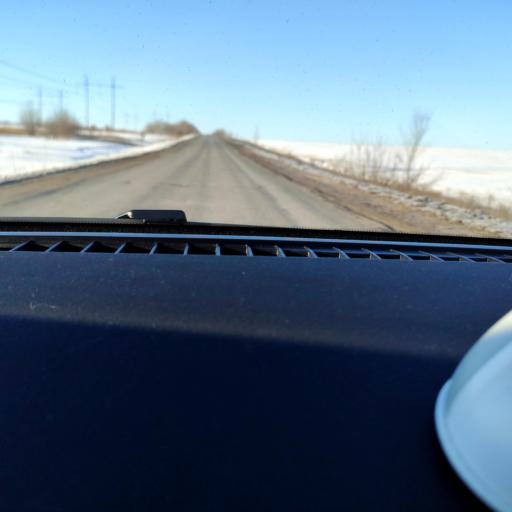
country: RU
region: Samara
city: Spiridonovka
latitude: 53.1443
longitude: 50.5459
